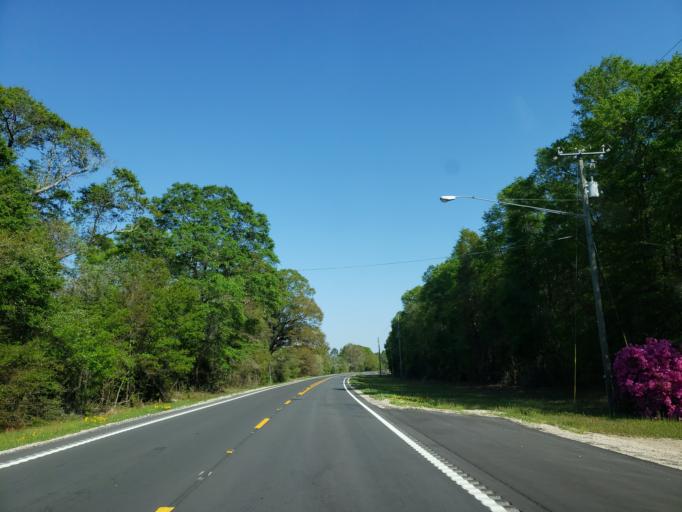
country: US
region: Mississippi
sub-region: Perry County
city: New Augusta
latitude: 31.1819
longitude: -88.9415
